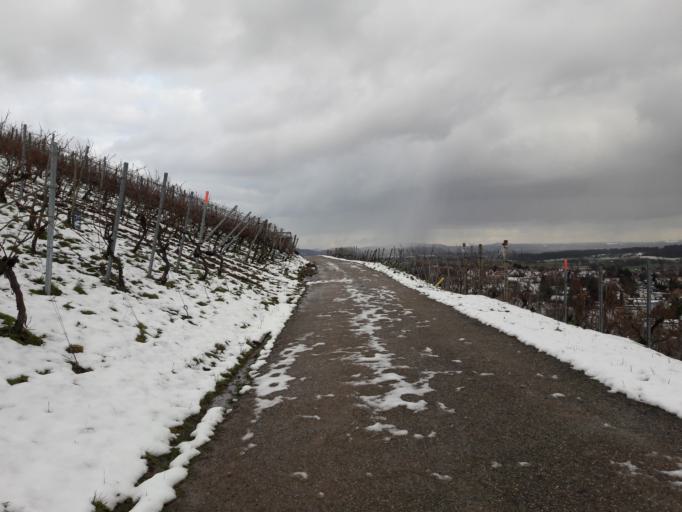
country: DE
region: Baden-Wuerttemberg
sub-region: Regierungsbezirk Stuttgart
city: Oberstenfeld
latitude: 48.9964
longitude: 9.3471
